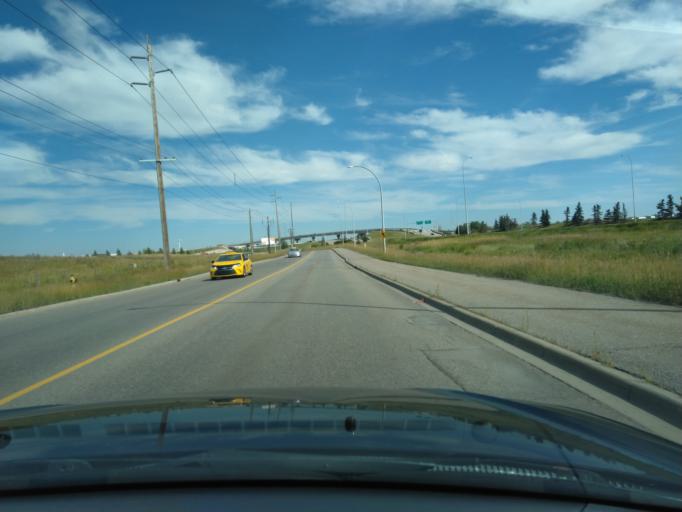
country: CA
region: Alberta
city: Calgary
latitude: 51.0959
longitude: -113.9919
